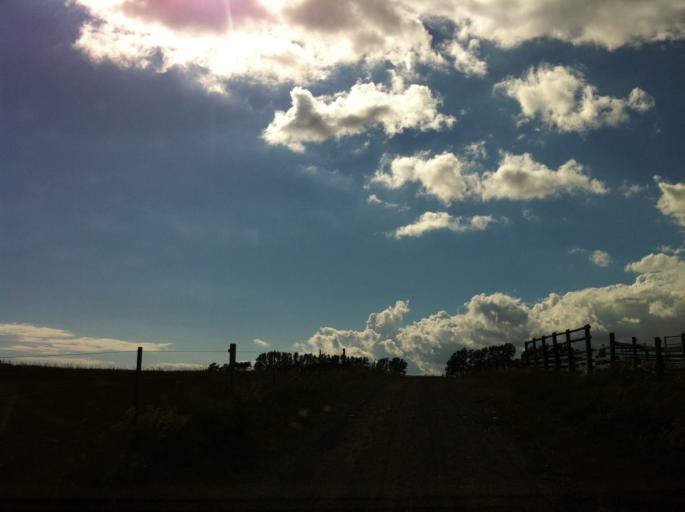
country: SE
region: Skane
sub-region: Ystads Kommun
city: Kopingebro
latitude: 55.3918
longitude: 14.0480
